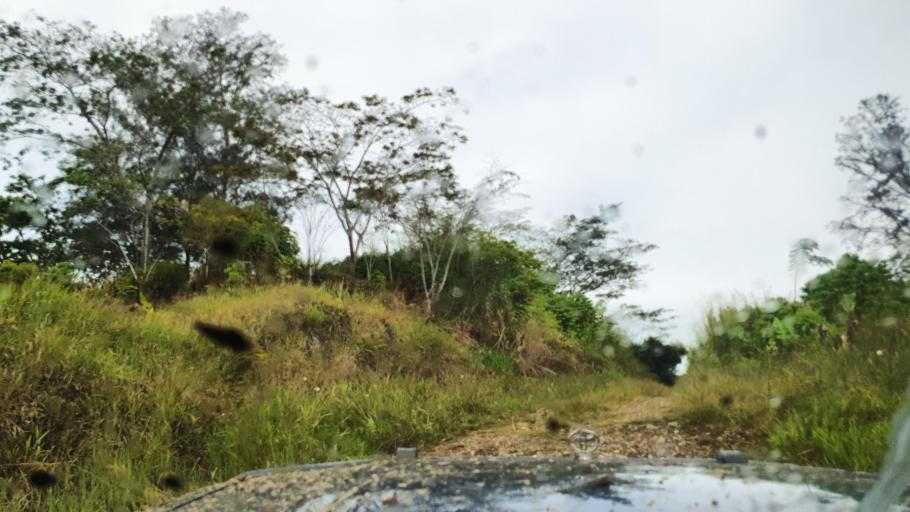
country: PG
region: Jiwaka
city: Minj
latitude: -5.9558
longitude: 144.7786
